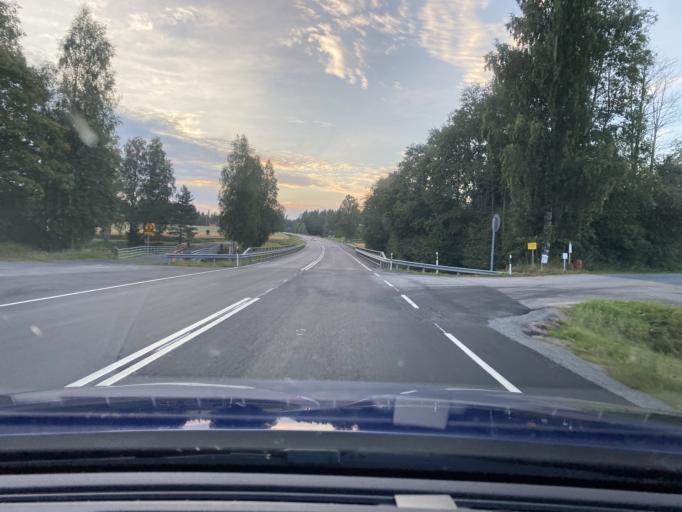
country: FI
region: Satakunta
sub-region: Pohjois-Satakunta
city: Kankaanpaeae
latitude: 61.8547
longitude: 22.3272
